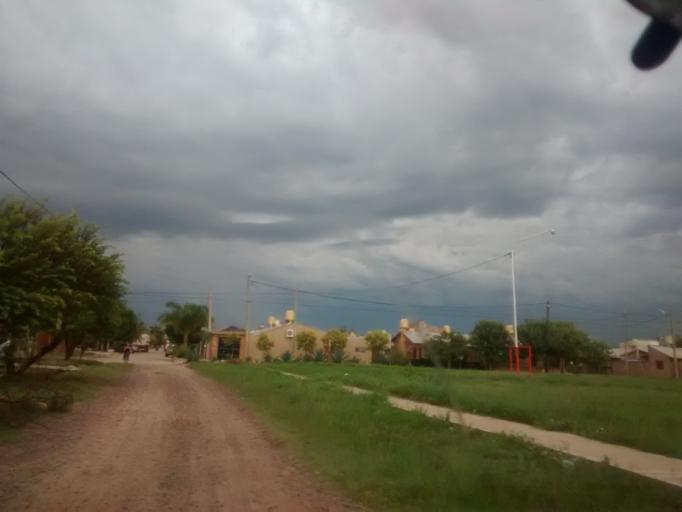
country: AR
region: Chaco
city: Fontana
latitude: -27.4503
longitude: -59.0242
